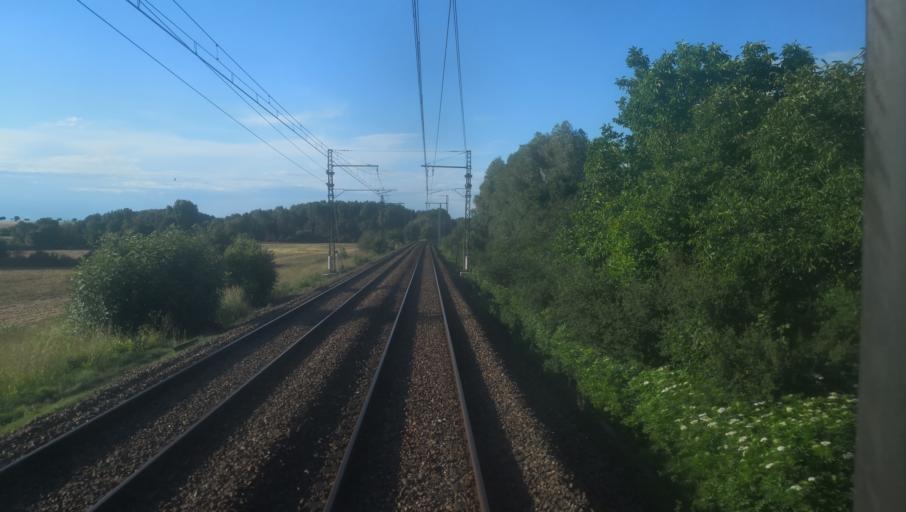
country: FR
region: Centre
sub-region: Departement de l'Indre
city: Sainte-Lizaigne
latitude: 47.0125
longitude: 2.0328
